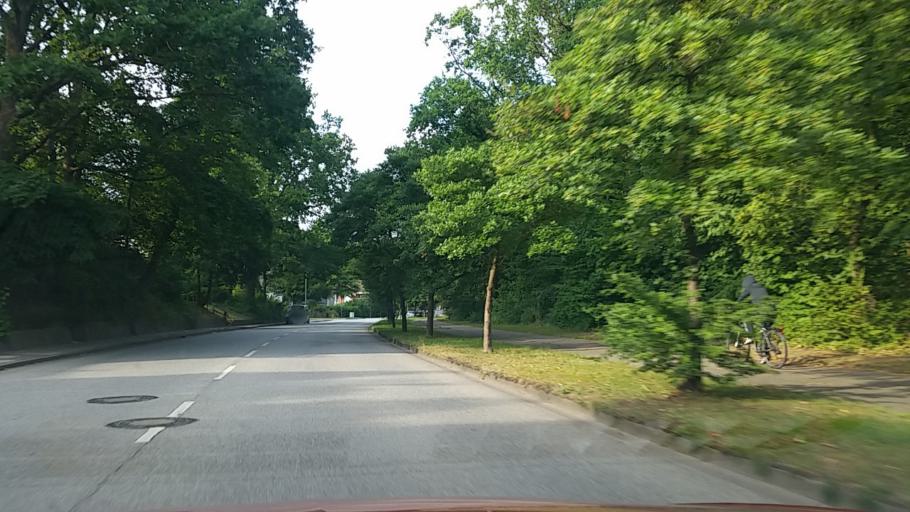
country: DE
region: Hamburg
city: Harburg
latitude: 53.4480
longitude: 9.9697
